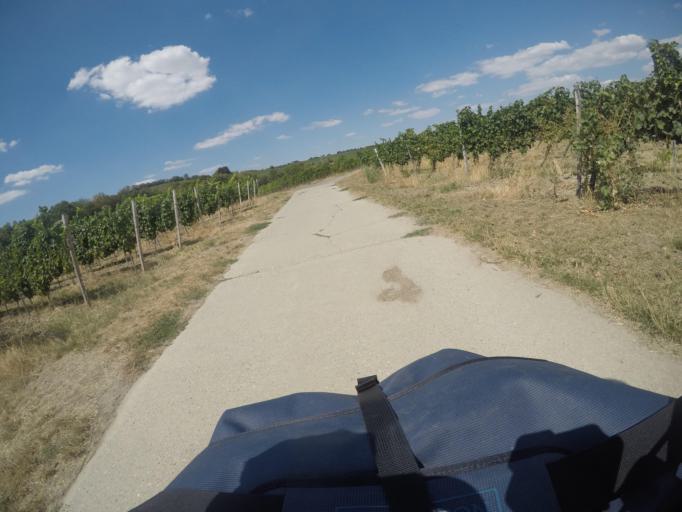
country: DE
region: Rheinland-Pfalz
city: Ludwigshohe
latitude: 49.8128
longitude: 8.3454
